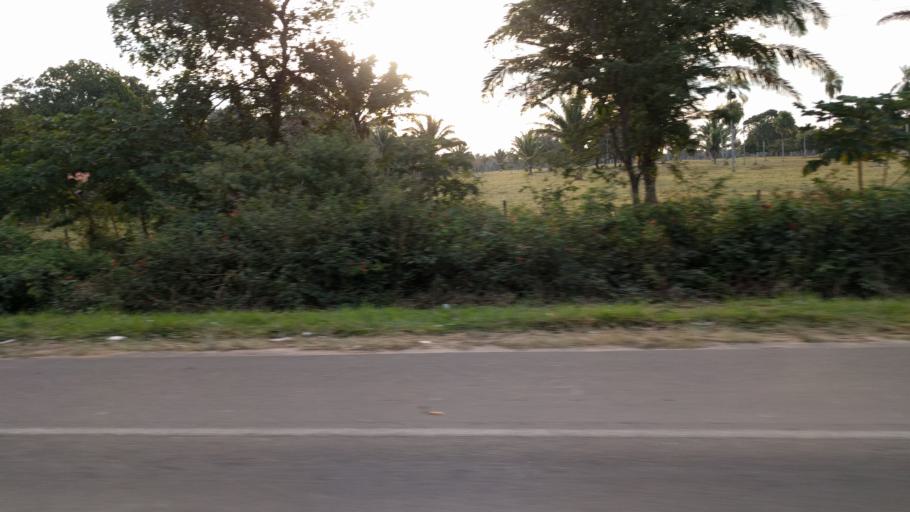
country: BO
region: Santa Cruz
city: Buena Vista
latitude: -17.4188
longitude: -63.6211
